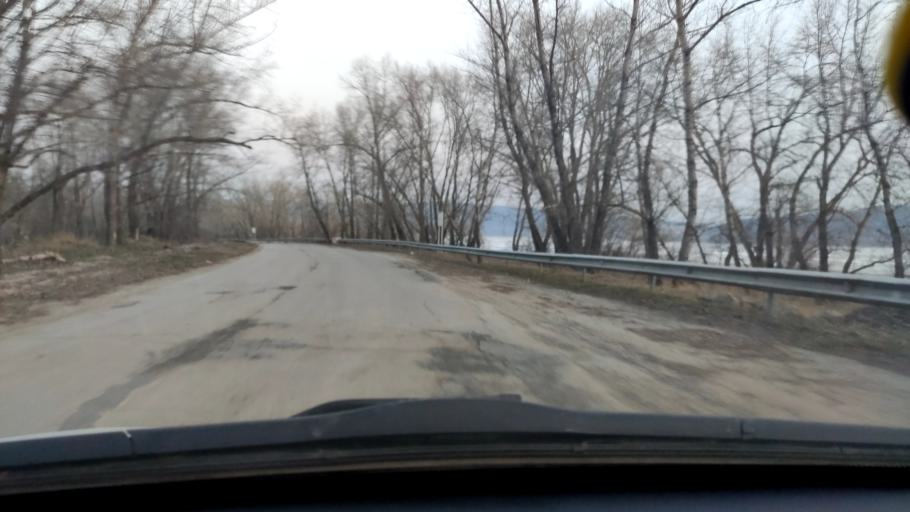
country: RU
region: Samara
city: Zhigulevsk
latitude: 53.4595
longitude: 49.5096
